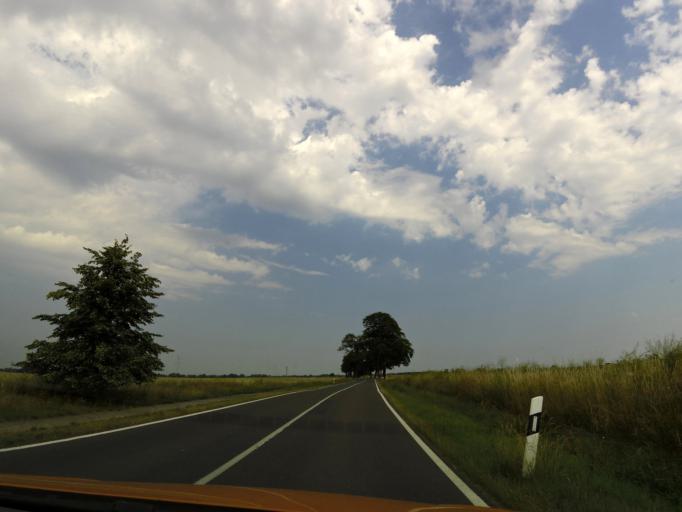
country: DE
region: Brandenburg
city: Nauen
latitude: 52.5607
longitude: 12.8693
